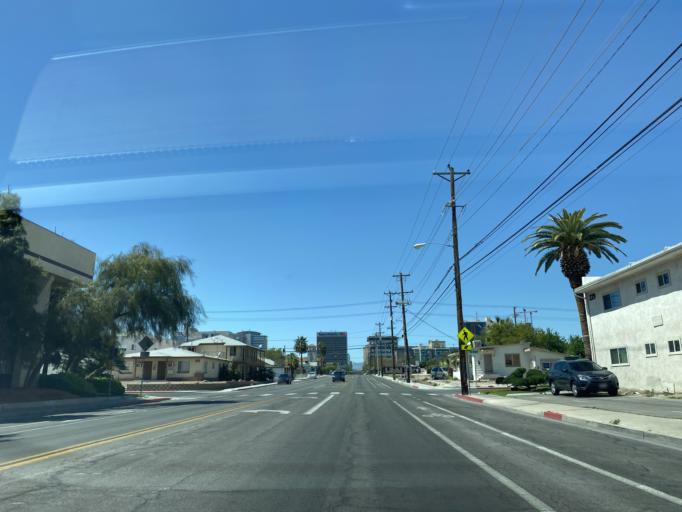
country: US
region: Nevada
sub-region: Clark County
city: Las Vegas
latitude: 36.1638
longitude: -115.1348
